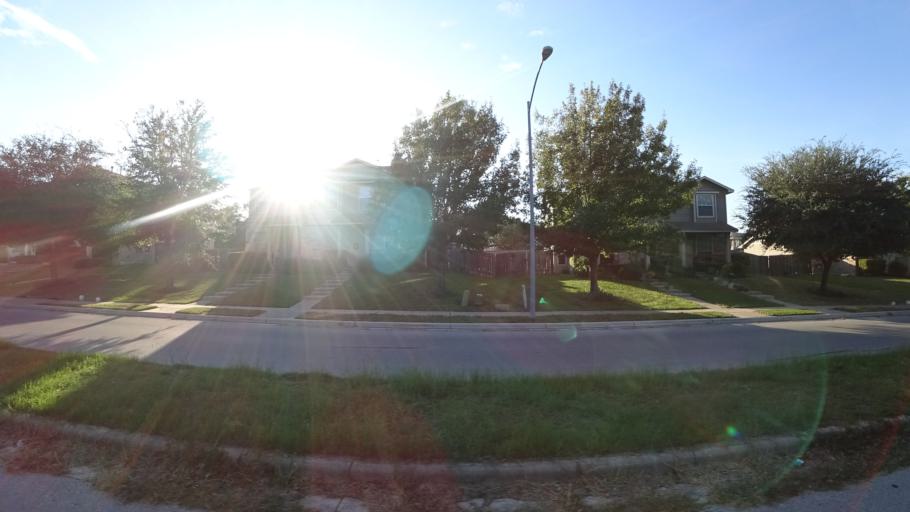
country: US
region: Texas
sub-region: Travis County
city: Pflugerville
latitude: 30.4171
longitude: -97.6466
